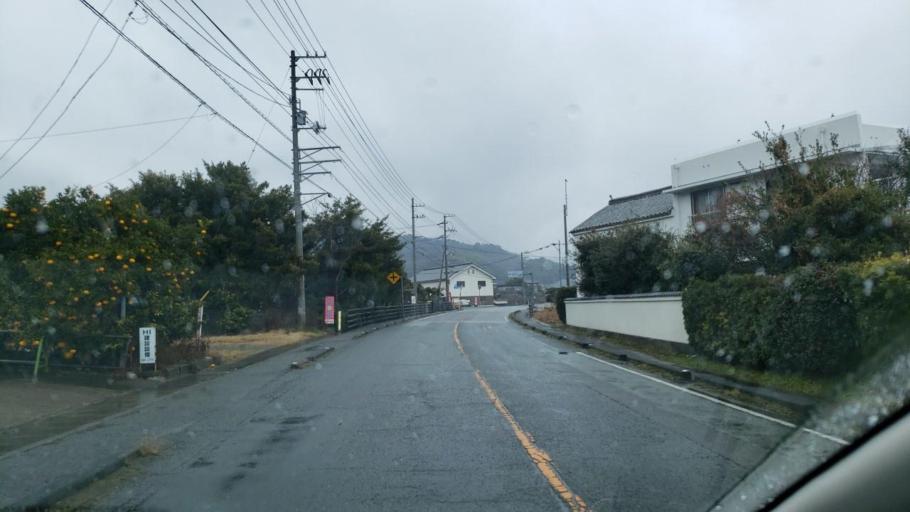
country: JP
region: Tokushima
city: Ishii
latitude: 34.1550
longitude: 134.4915
